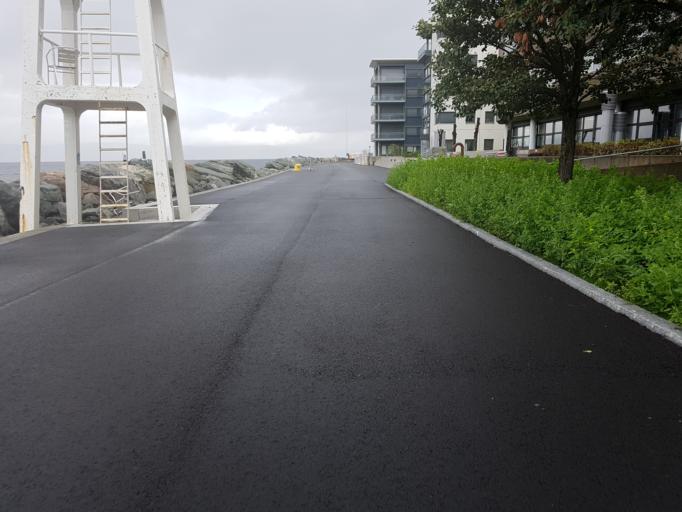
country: NO
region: Sor-Trondelag
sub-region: Trondheim
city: Trondheim
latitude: 63.4418
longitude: 10.4021
